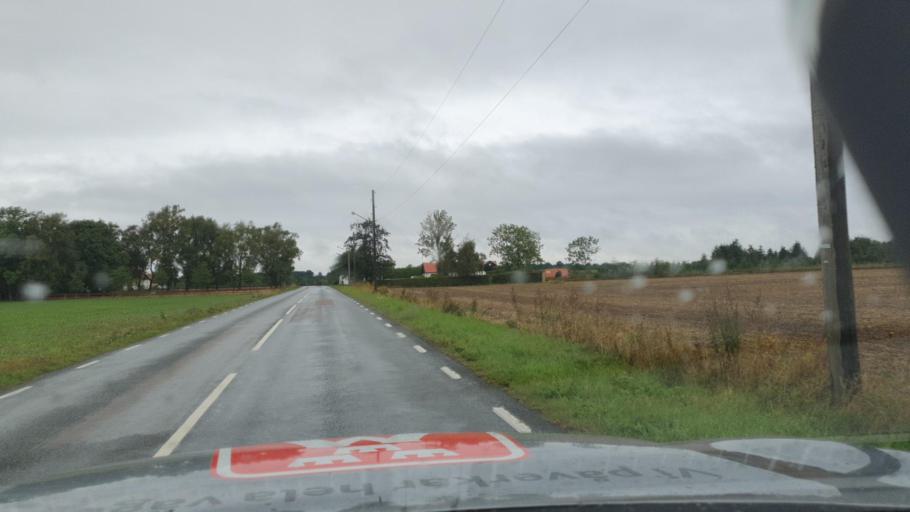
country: SE
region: Skane
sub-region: Simrishamns Kommun
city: Kivik
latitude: 55.5679
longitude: 14.1541
